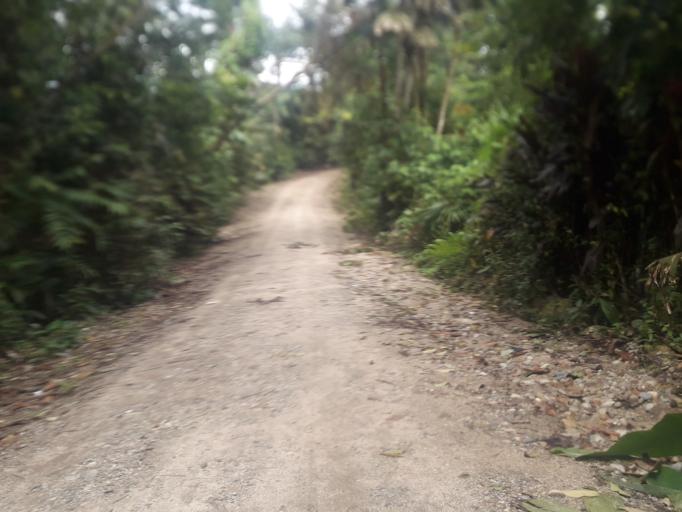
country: EC
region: Napo
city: Tena
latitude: -0.9736
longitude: -77.8423
